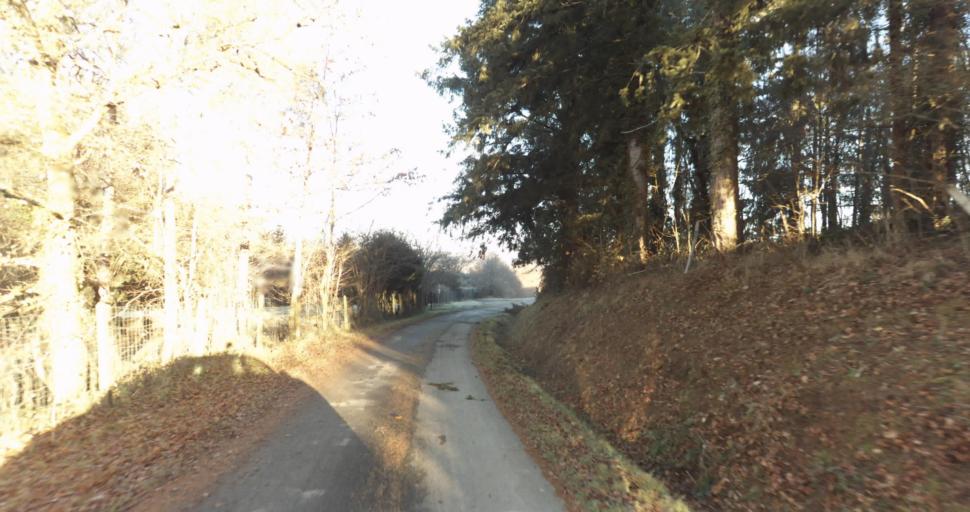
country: FR
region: Limousin
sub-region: Departement de la Haute-Vienne
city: Aixe-sur-Vienne
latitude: 45.8218
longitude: 1.1441
